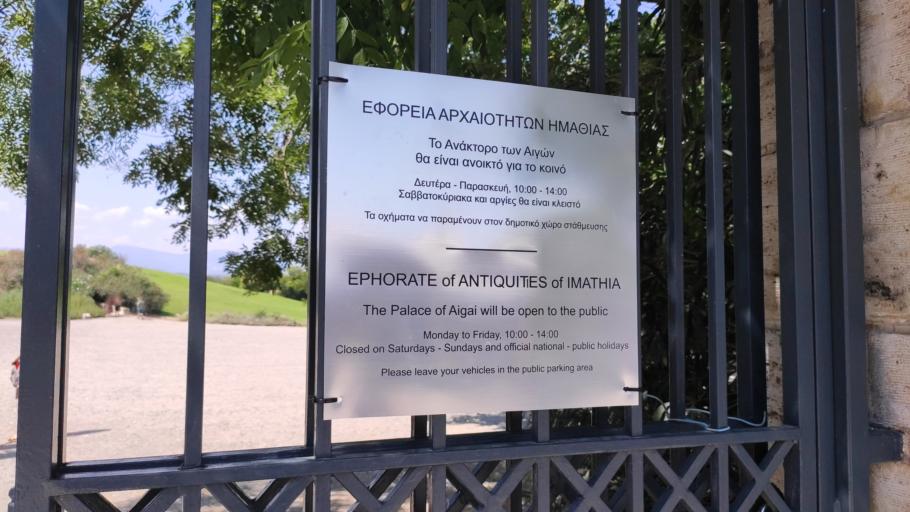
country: GR
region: Central Macedonia
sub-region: Nomos Imathias
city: Vergina
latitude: 40.4875
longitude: 22.3210
